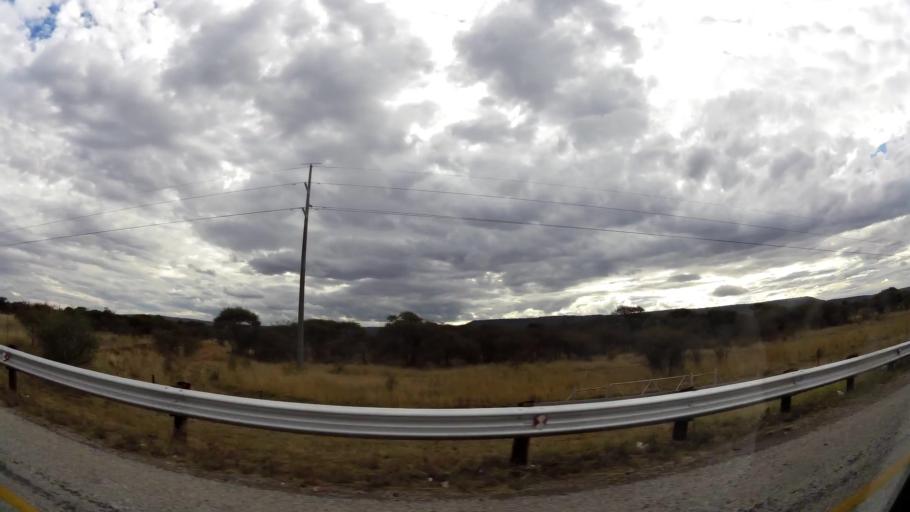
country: ZA
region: Limpopo
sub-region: Waterberg District Municipality
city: Modimolle
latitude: -24.5652
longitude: 28.6818
